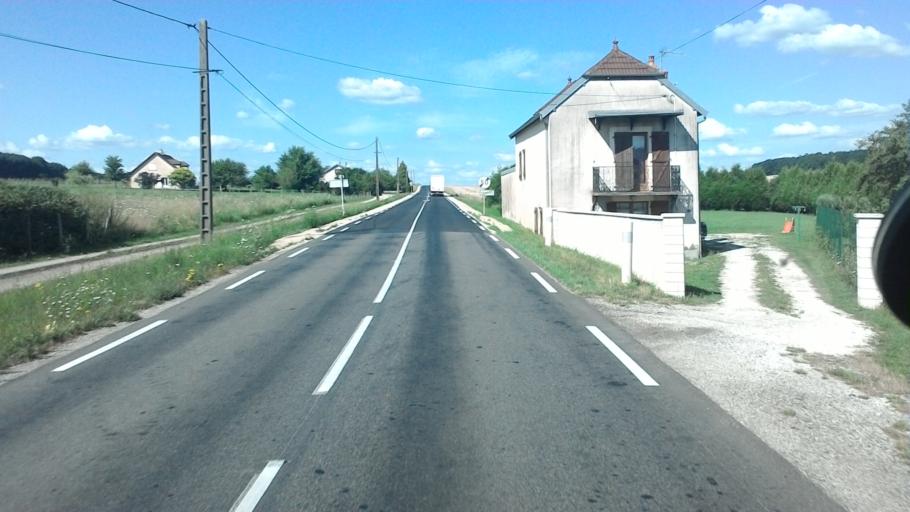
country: FR
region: Franche-Comte
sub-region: Departement de la Haute-Saone
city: Marnay
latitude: 47.3230
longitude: 5.6834
